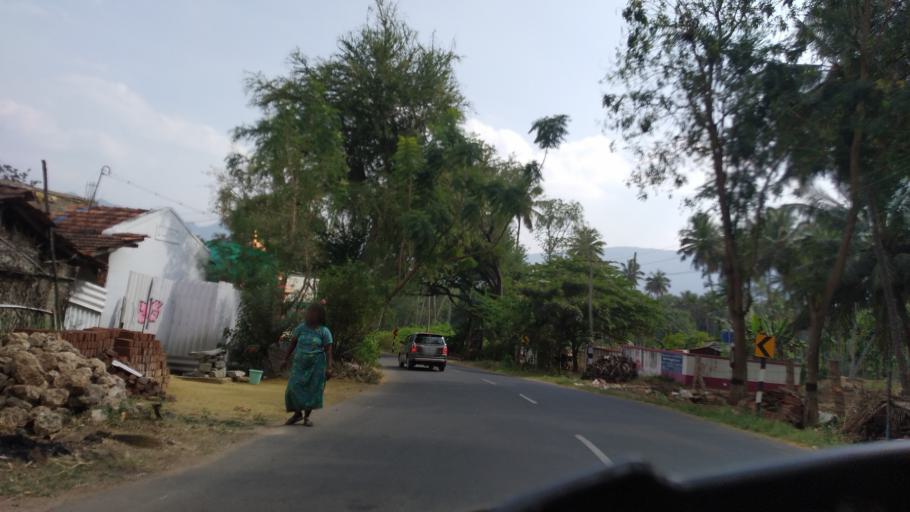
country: IN
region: Tamil Nadu
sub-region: Coimbatore
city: Perur
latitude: 10.9520
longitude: 76.7635
